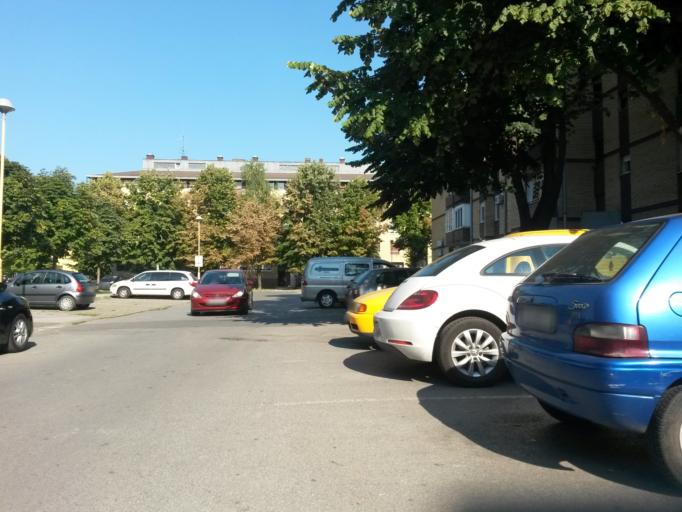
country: HR
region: Osjecko-Baranjska
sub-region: Grad Osijek
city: Osijek
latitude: 45.5501
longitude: 18.7005
